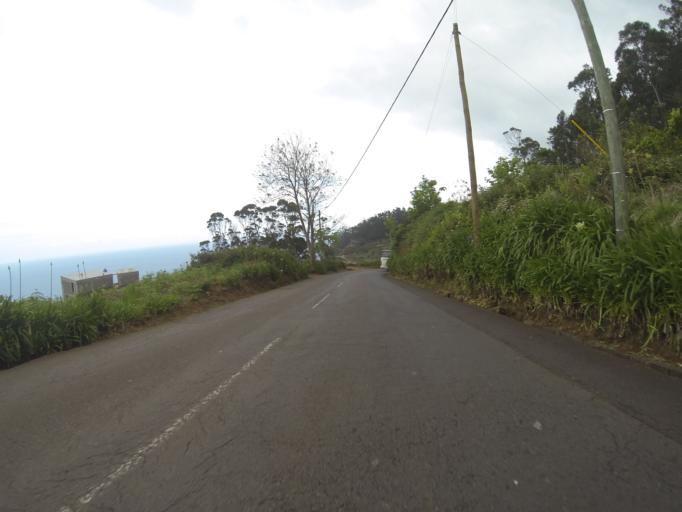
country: PT
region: Madeira
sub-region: Porto Moniz
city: Porto Moniz
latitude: 32.8607
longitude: -17.1710
